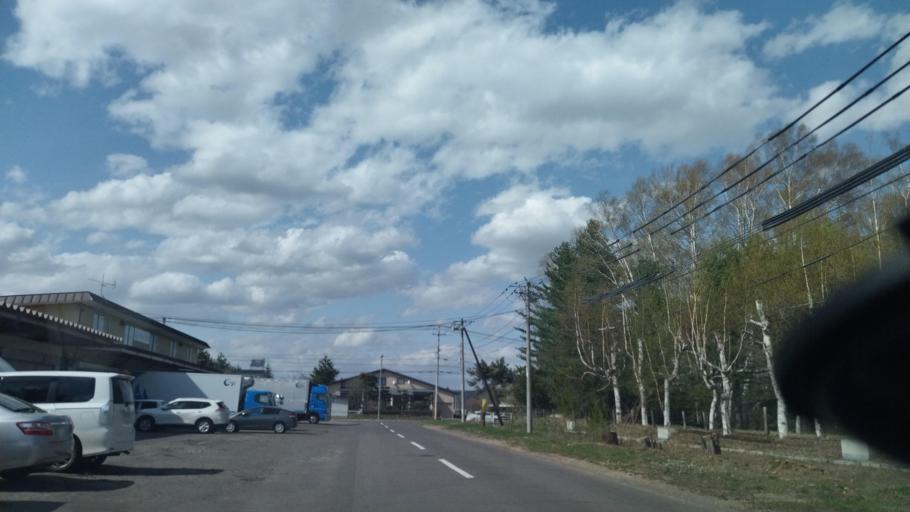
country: JP
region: Hokkaido
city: Obihiro
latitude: 42.9313
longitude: 143.1354
